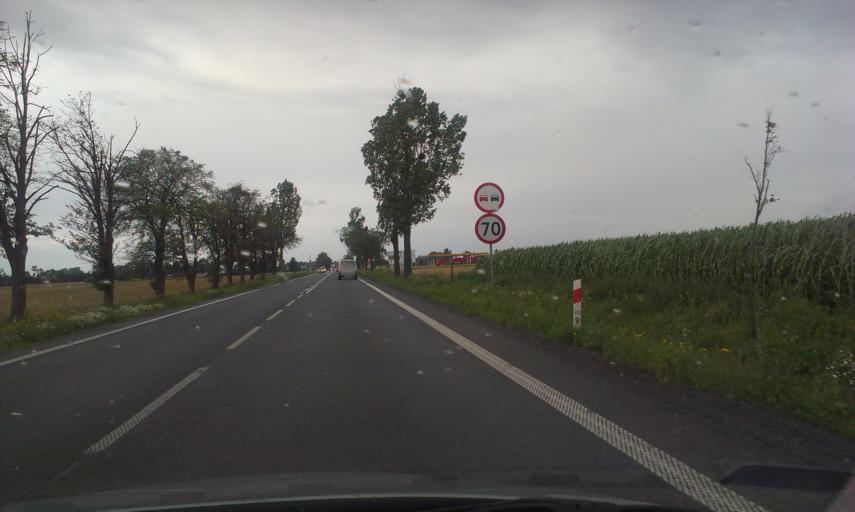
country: PL
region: Greater Poland Voivodeship
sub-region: Powiat obornicki
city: Oborniki
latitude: 52.6155
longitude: 16.8138
